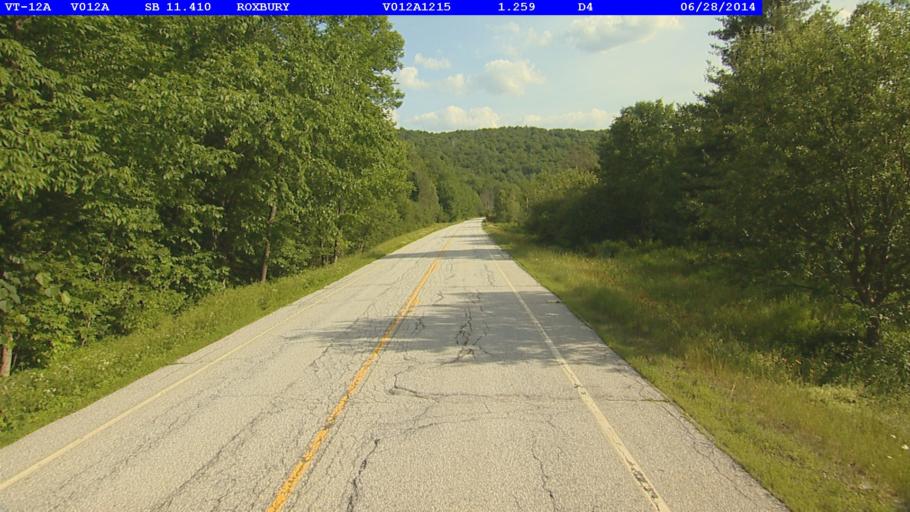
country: US
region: Vermont
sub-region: Washington County
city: Northfield
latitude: 44.0468
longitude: -72.7428
